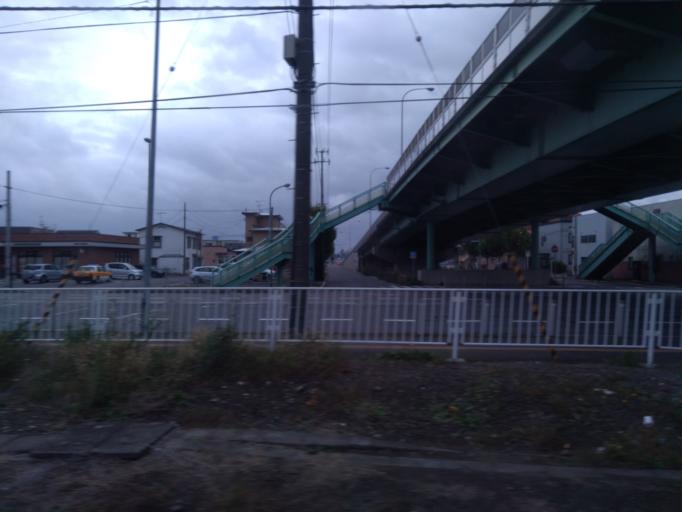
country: JP
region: Hokkaido
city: Hakodate
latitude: 41.8007
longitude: 140.7340
